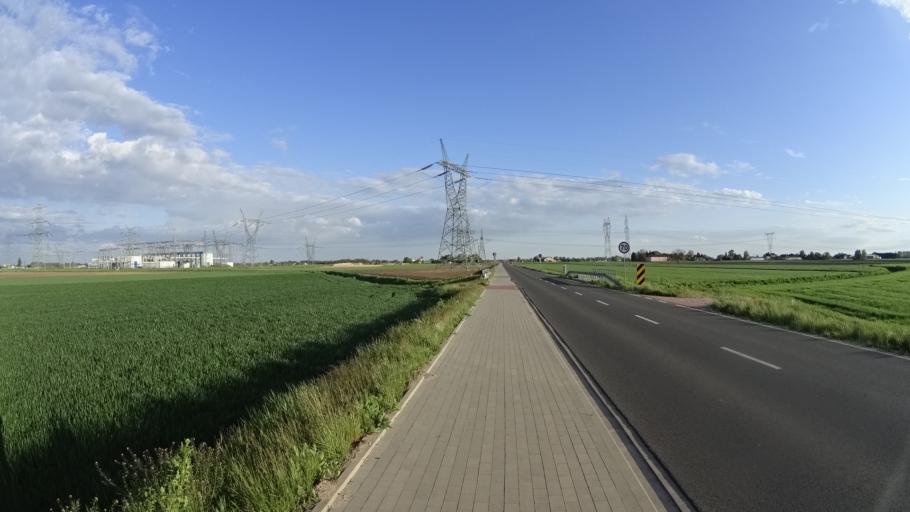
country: PL
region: Masovian Voivodeship
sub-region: Powiat warszawski zachodni
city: Jozefow
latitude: 52.2298
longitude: 20.7377
